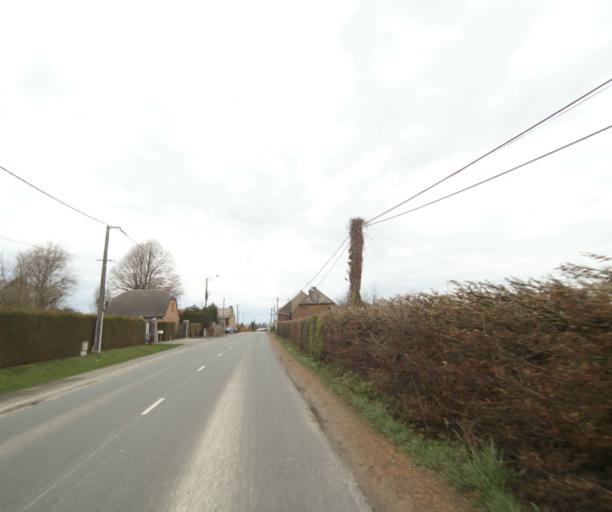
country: FR
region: Nord-Pas-de-Calais
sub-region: Departement du Nord
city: Sebourg
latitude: 50.3451
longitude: 3.6391
